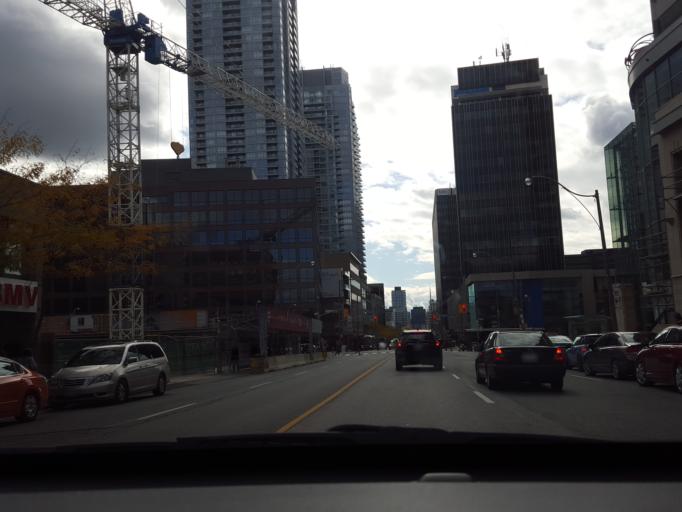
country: CA
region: Ontario
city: Toronto
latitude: 43.7077
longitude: -79.3986
